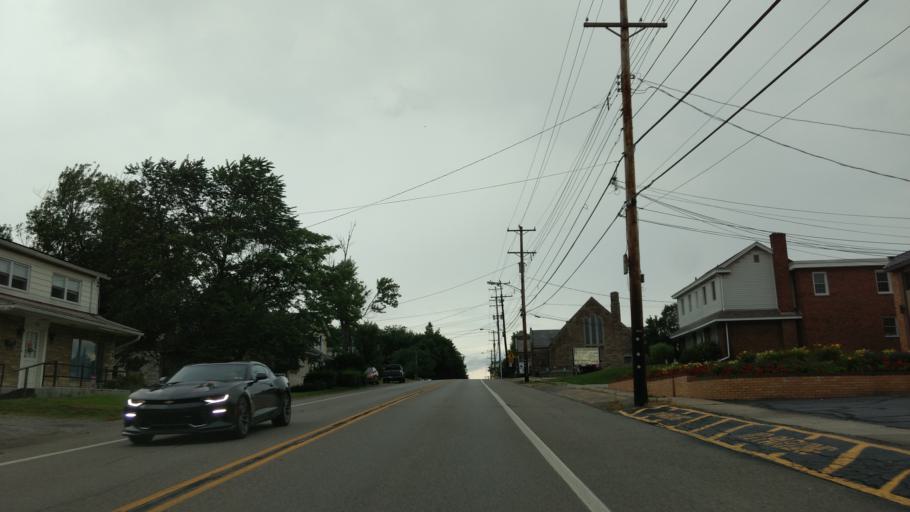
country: US
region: Pennsylvania
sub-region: Allegheny County
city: West View
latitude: 40.5322
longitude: -80.0358
